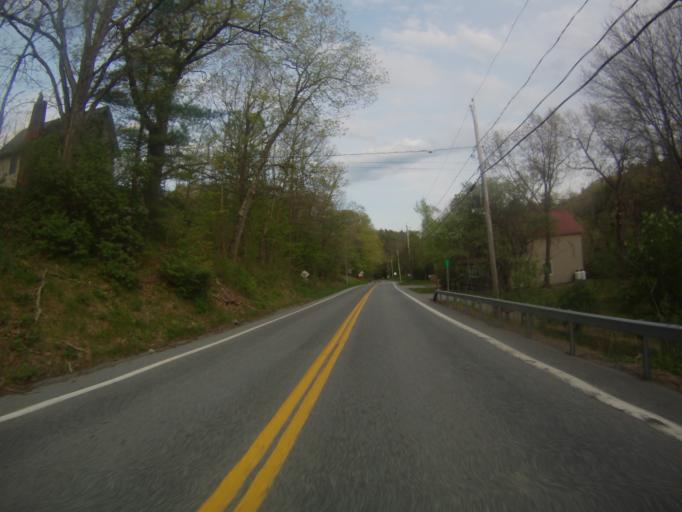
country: US
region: New York
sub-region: Essex County
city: Ticonderoga
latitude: 43.7539
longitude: -73.5069
